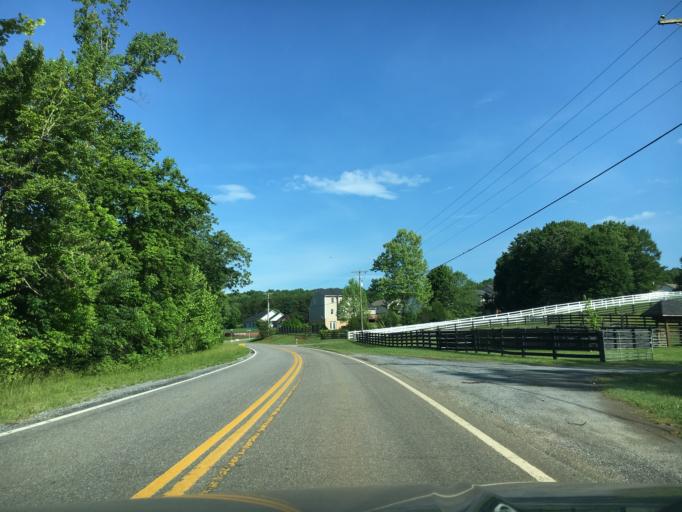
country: US
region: Virginia
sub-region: Campbell County
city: Rustburg
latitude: 37.3119
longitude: -79.1726
